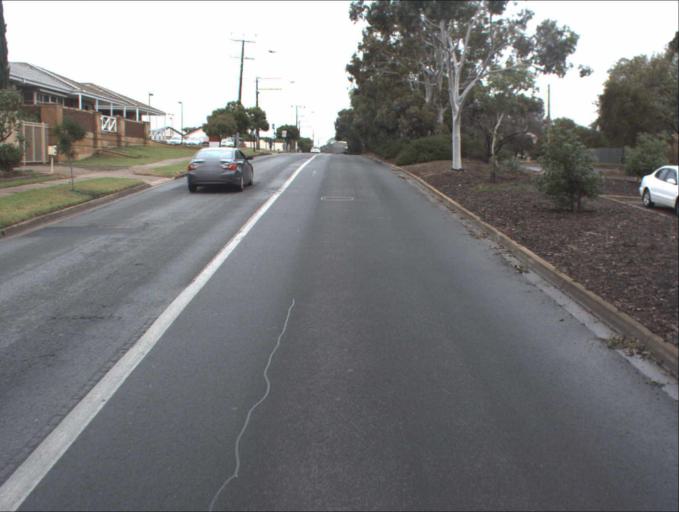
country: AU
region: South Australia
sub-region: Port Adelaide Enfield
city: Gilles Plains
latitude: -34.8398
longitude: 138.6627
